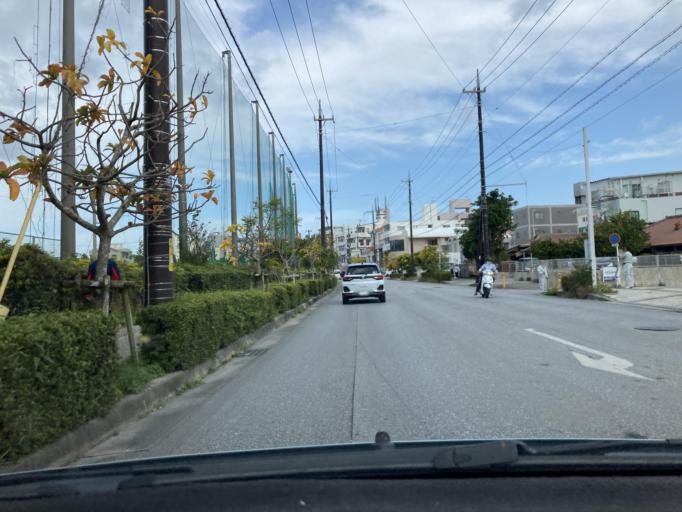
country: JP
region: Okinawa
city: Naha-shi
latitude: 26.2318
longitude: 127.6951
